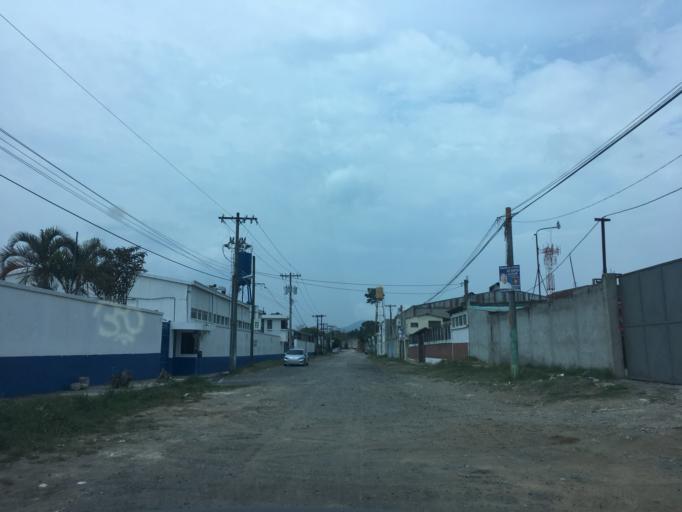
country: GT
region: Guatemala
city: Petapa
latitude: 14.5081
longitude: -90.5561
